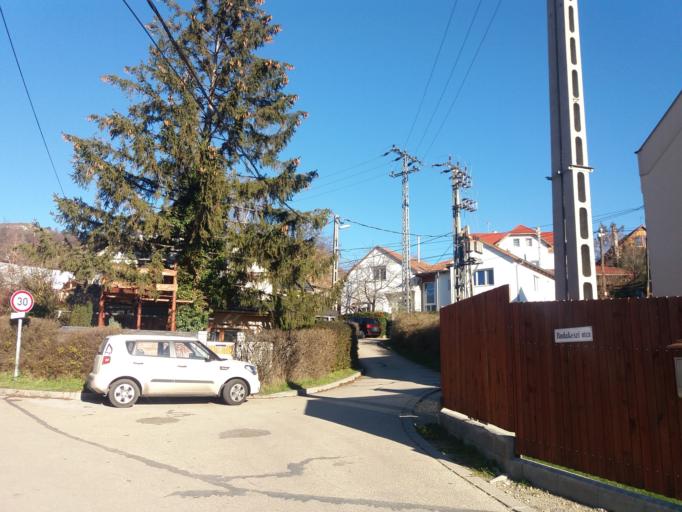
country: HU
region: Pest
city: Budaors
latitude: 47.4664
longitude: 18.9528
